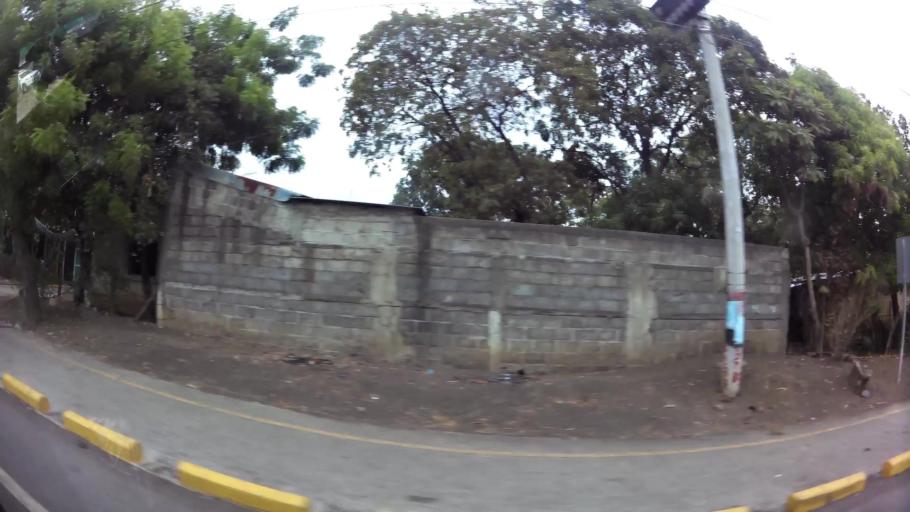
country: NI
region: Leon
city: Leon
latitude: 12.4522
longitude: -86.8639
